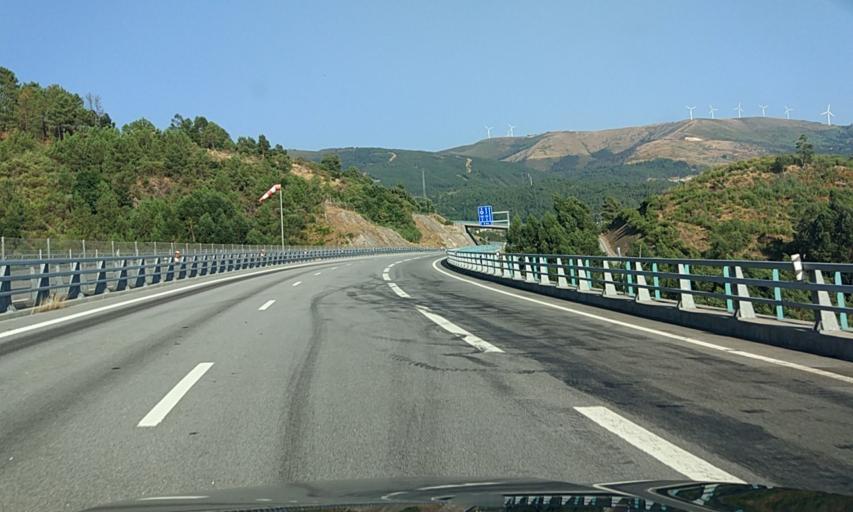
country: PT
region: Porto
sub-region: Amarante
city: Amarante
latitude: 41.2569
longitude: -7.9799
